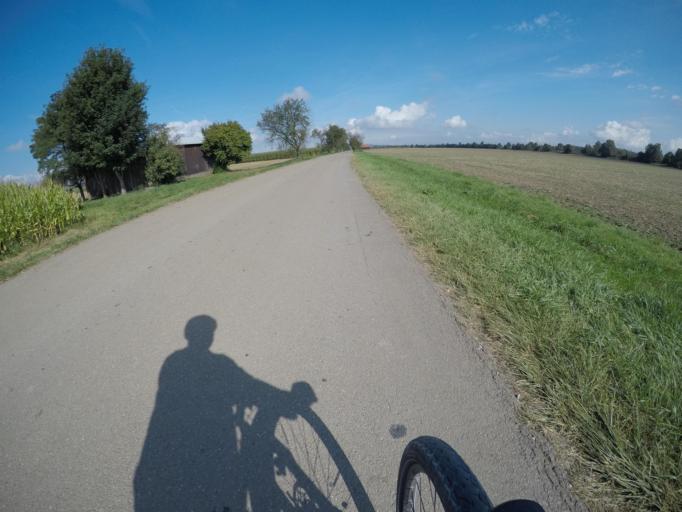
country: DE
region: Bavaria
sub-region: Swabia
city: Buttenwiesen
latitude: 48.6317
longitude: 10.7398
